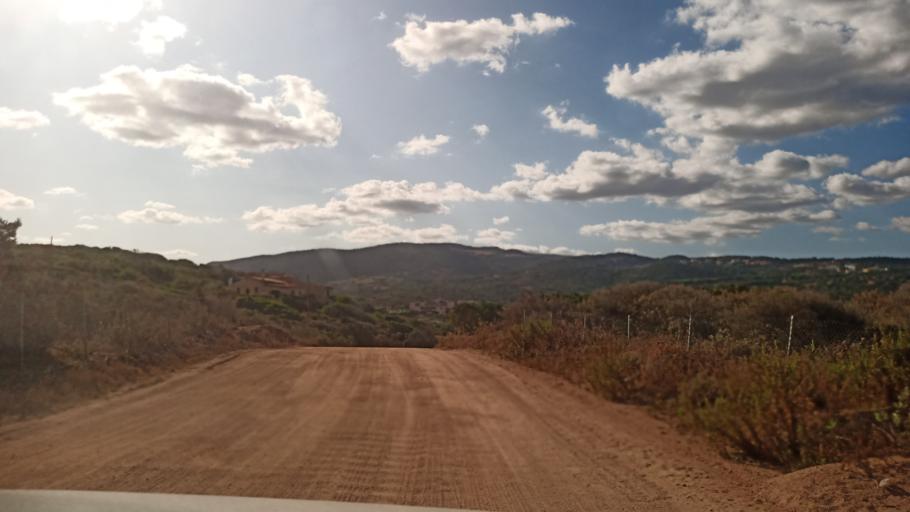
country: IT
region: Sardinia
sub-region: Provincia di Olbia-Tempio
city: Trinita d'Agultu
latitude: 41.0194
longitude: 8.8901
